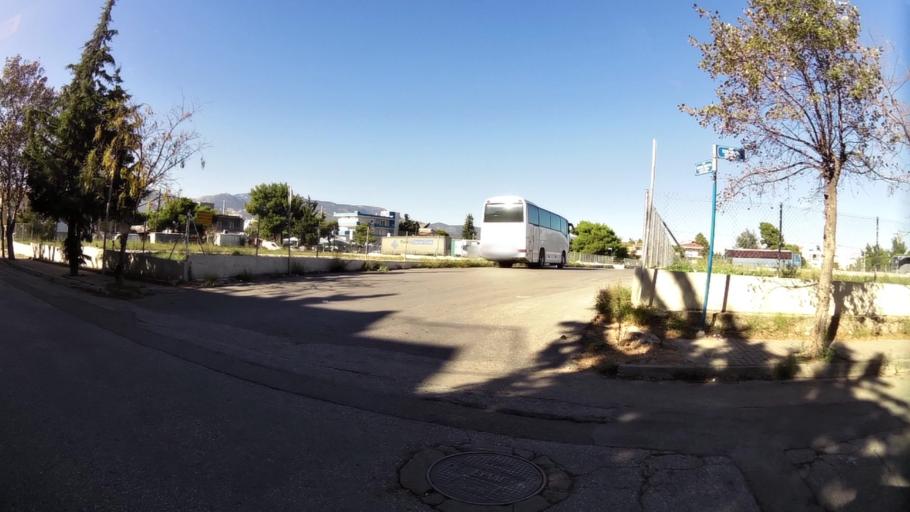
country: GR
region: Attica
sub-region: Nomarchia Athinas
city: Nea Erythraia
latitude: 38.0969
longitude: 23.8110
